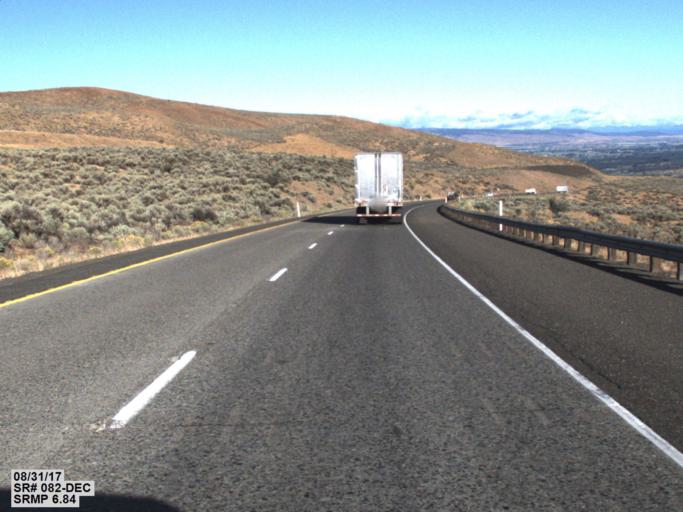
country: US
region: Washington
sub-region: Kittitas County
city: Kittitas
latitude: 46.8932
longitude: -120.4410
